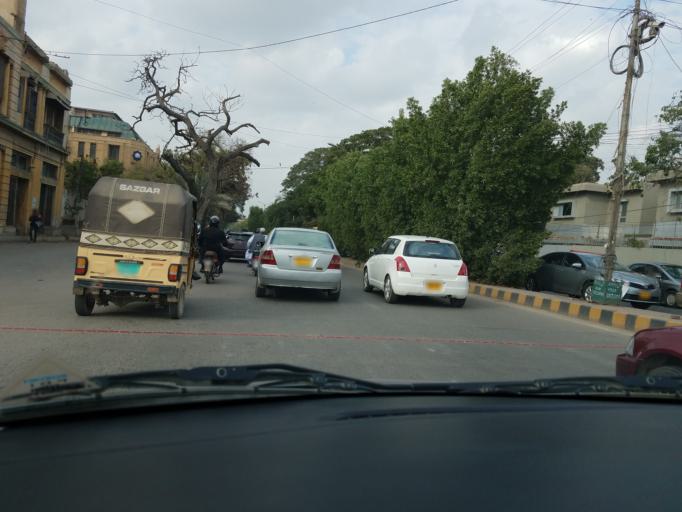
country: PK
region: Sindh
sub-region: Karachi District
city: Karachi
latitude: 24.8439
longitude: 67.0322
